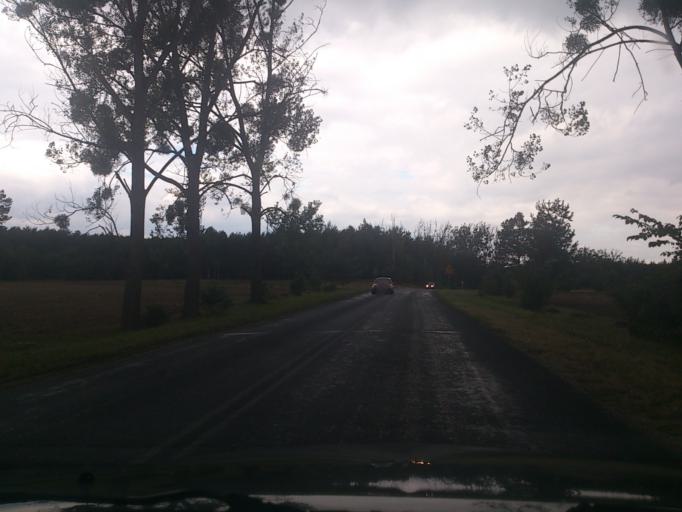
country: PL
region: Kujawsko-Pomorskie
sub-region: Powiat golubsko-dobrzynski
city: Golub-Dobrzyn
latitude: 53.0884
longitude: 19.0527
